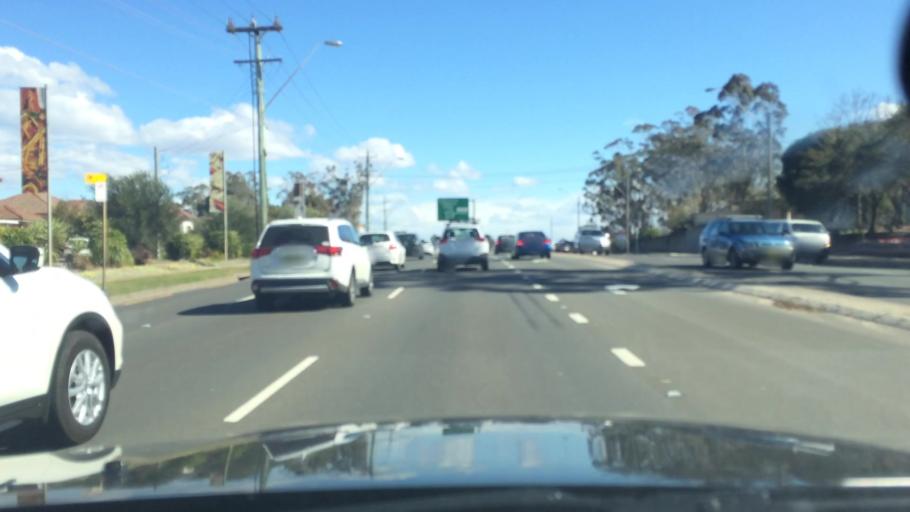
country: AU
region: New South Wales
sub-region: Campbelltown Municipality
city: Glenfield
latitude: -33.9570
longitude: 150.8899
